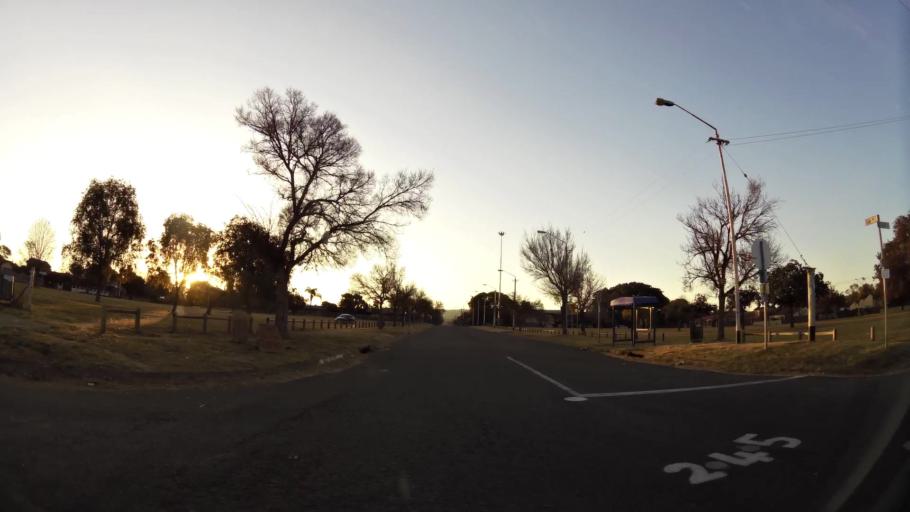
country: ZA
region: Gauteng
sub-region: City of Tshwane Metropolitan Municipality
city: Pretoria
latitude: -25.7452
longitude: 28.1312
